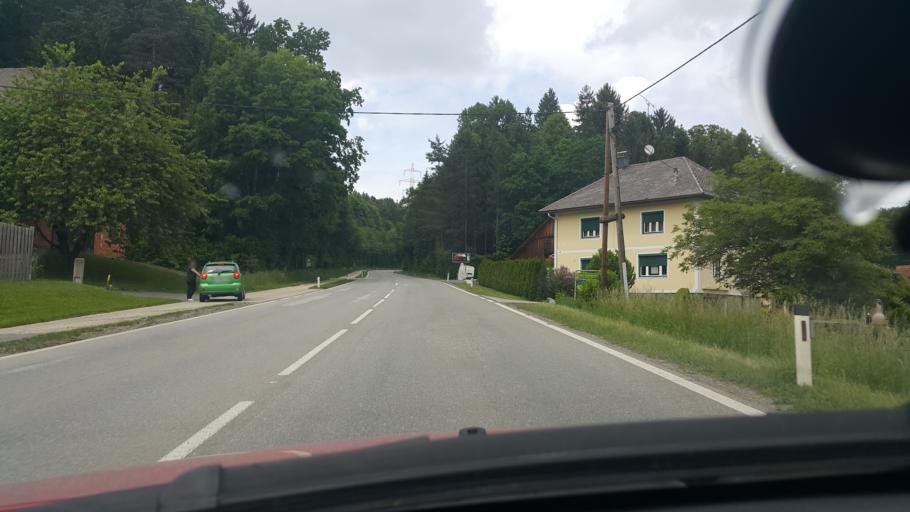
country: AT
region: Styria
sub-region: Politischer Bezirk Leibnitz
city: Weitendorf
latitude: 46.8685
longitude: 15.4776
